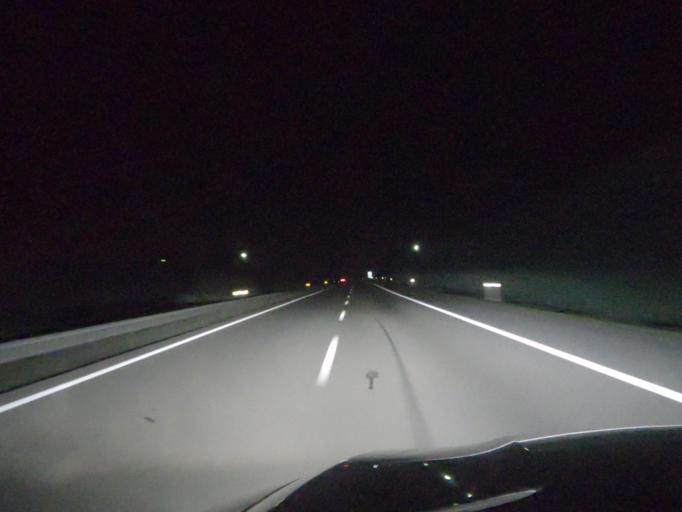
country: PT
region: Aveiro
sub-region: Mealhada
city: Mealhada
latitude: 40.3812
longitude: -8.4914
